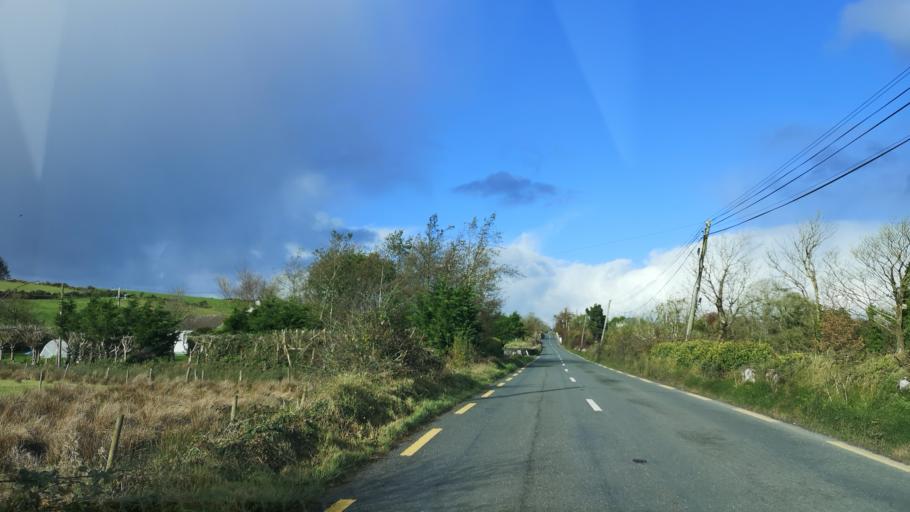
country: IE
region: Connaught
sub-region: Maigh Eo
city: Castlebar
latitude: 53.7666
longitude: -9.3811
